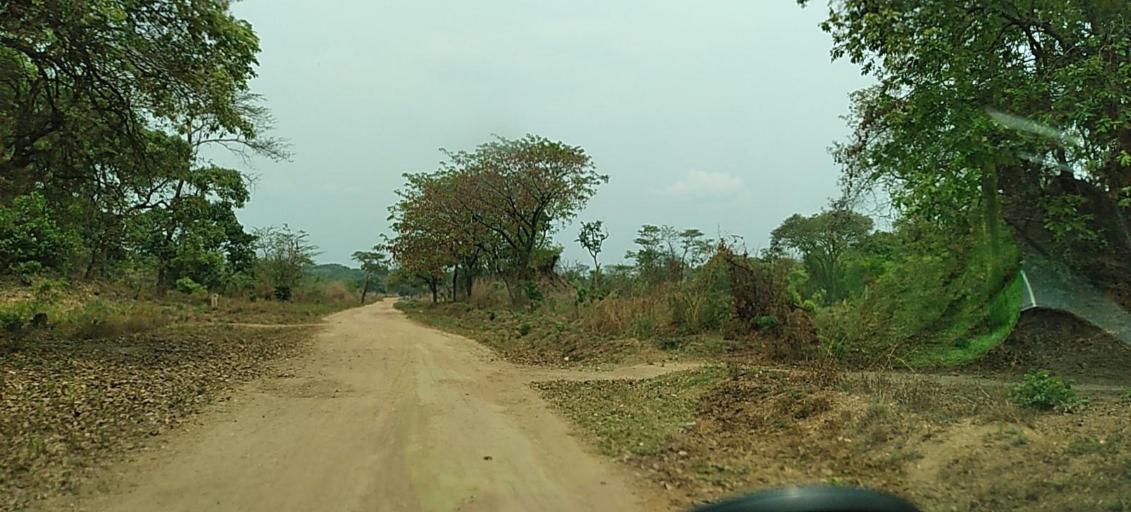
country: ZM
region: North-Western
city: Solwezi
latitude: -12.7912
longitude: 26.5301
